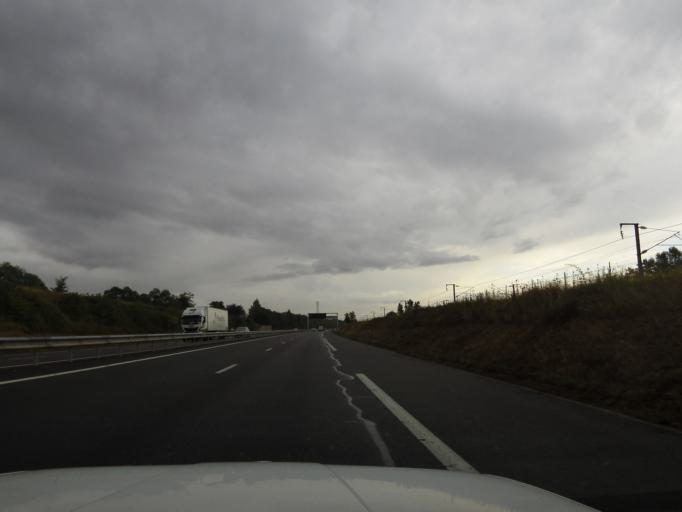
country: FR
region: Rhone-Alpes
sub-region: Departement du Rhone
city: Jons
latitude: 45.7966
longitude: 5.0778
